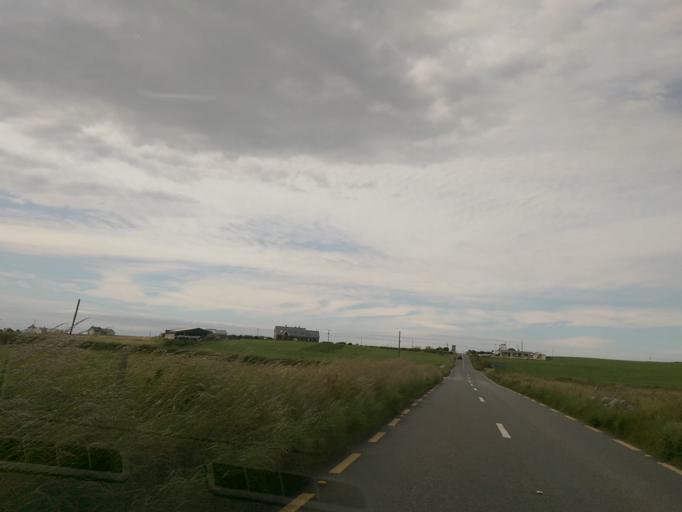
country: IE
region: Munster
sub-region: An Clar
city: Kilrush
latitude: 52.8640
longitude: -9.4123
